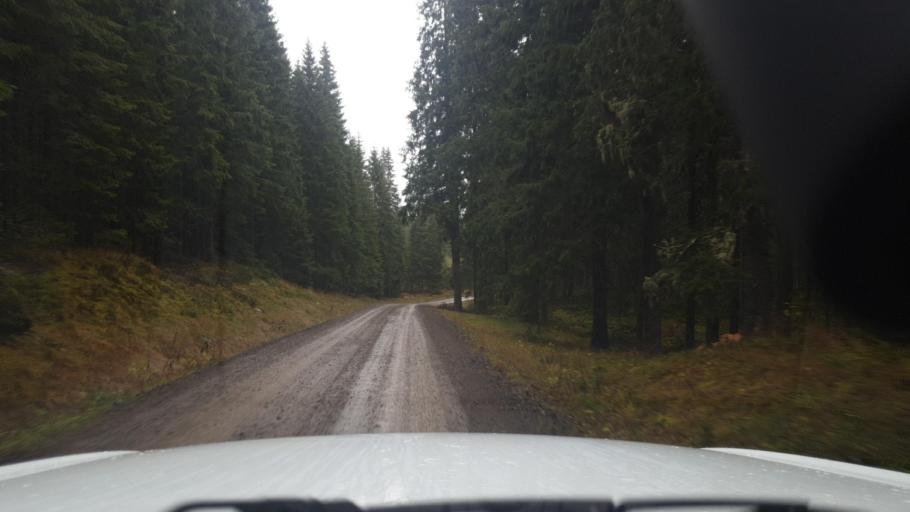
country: SE
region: Vaermland
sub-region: Sunne Kommun
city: Sunne
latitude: 59.8594
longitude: 12.8651
